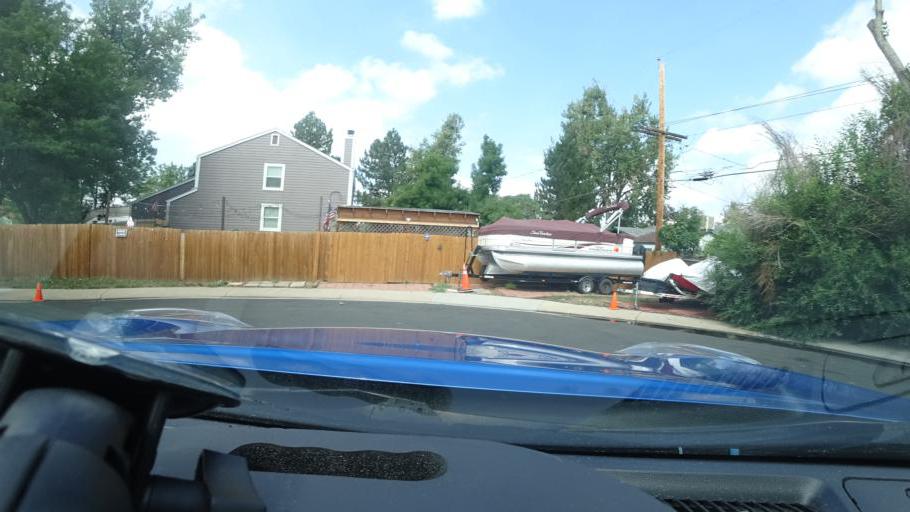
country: US
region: Colorado
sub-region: Adams County
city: Aurora
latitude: 39.7183
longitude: -104.8549
